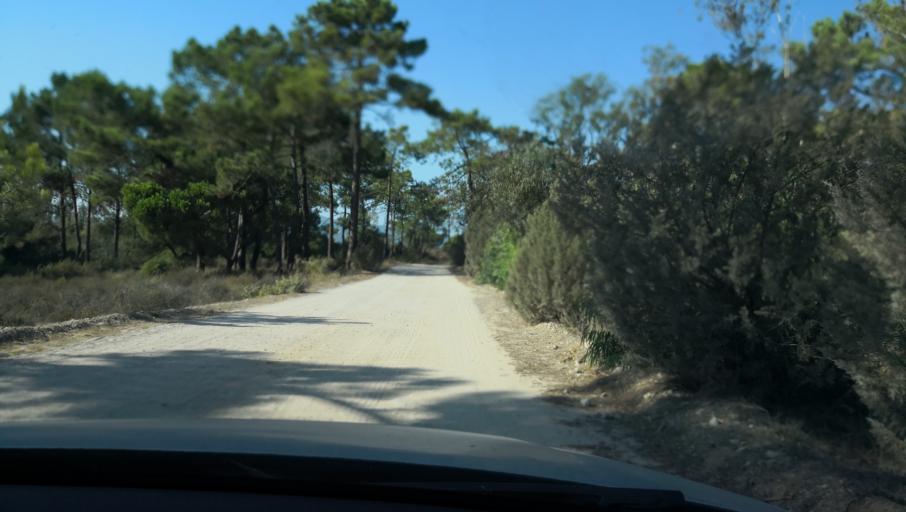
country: PT
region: Setubal
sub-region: Setubal
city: Setubal
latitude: 38.4725
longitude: -8.8784
